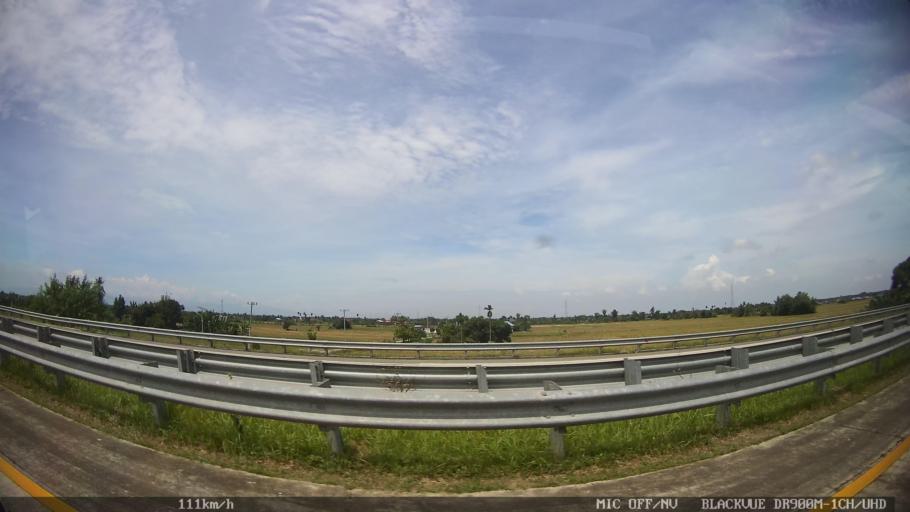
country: ID
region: North Sumatra
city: Percut
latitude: 3.5737
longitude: 98.8473
